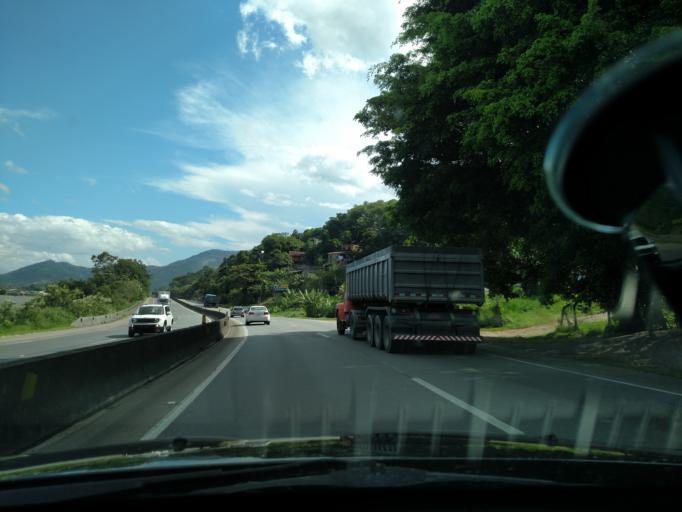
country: BR
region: Santa Catarina
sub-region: Biguacu
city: Biguacu
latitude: -27.4789
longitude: -48.6440
